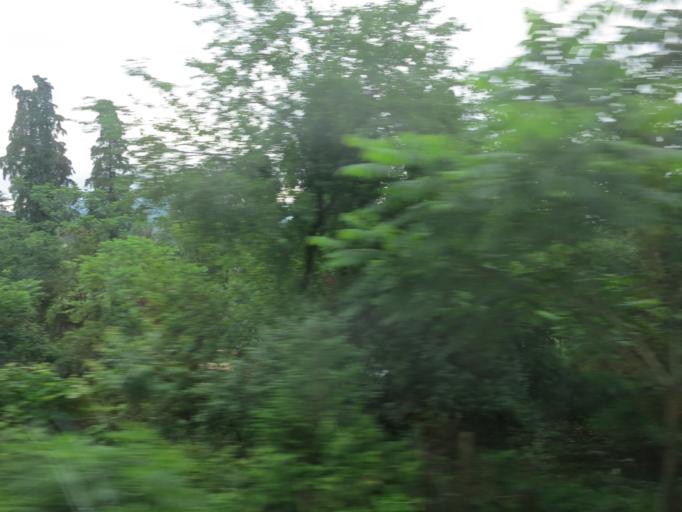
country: GE
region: Ajaria
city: Makhinjauri
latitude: 41.7192
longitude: 41.7286
